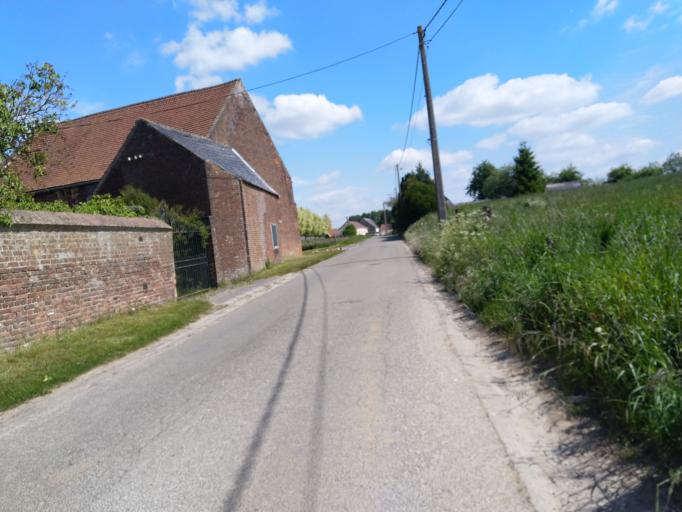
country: BE
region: Wallonia
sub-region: Province du Hainaut
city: Soignies
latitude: 50.5609
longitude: 4.0168
